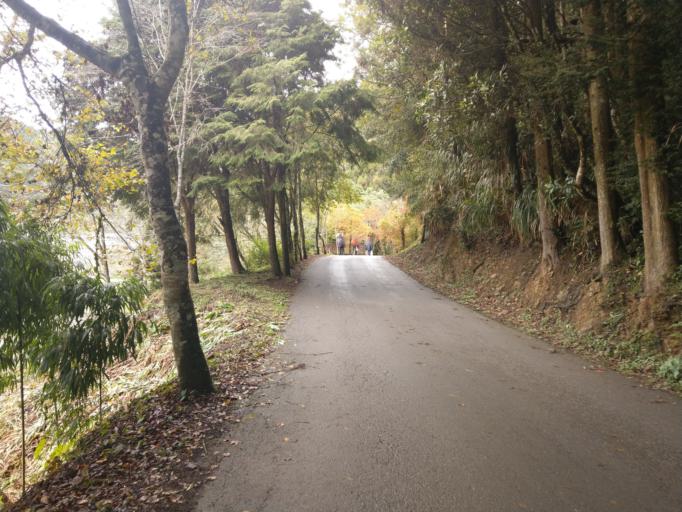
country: TW
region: Taiwan
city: Lugu
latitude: 23.6352
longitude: 120.7940
